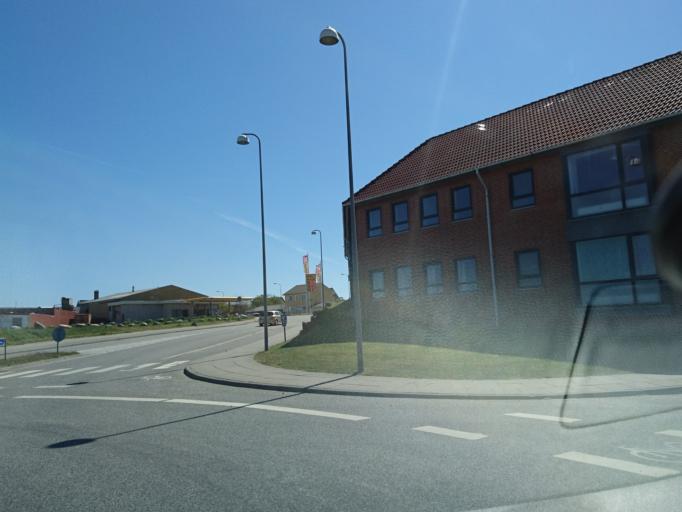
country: DK
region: North Denmark
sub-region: Hjorring Kommune
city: Hirtshals
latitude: 57.5902
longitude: 9.9635
